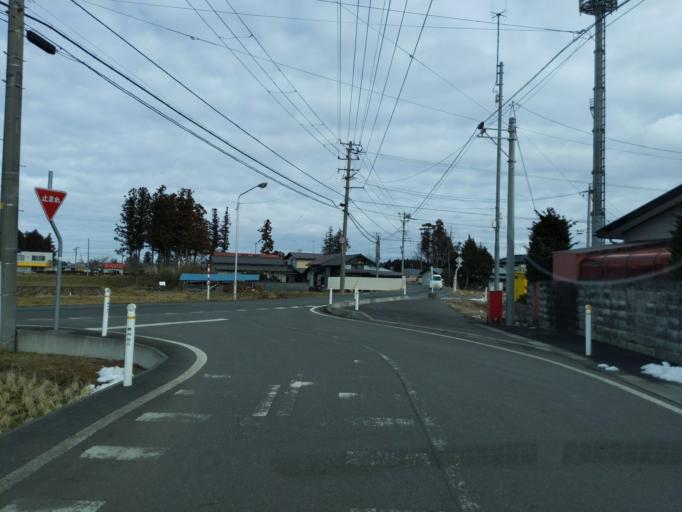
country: JP
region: Iwate
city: Mizusawa
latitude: 39.0933
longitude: 141.1774
